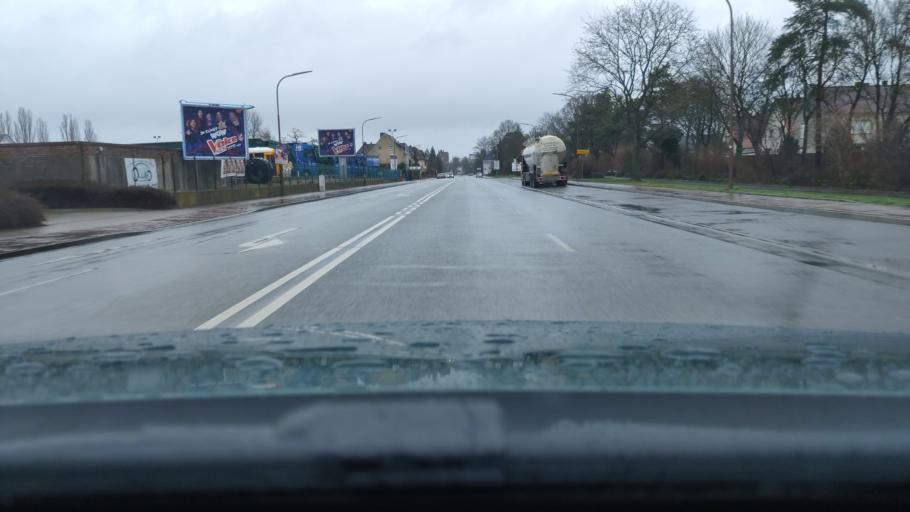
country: DE
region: Lower Saxony
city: Peine
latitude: 52.3100
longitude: 10.2326
